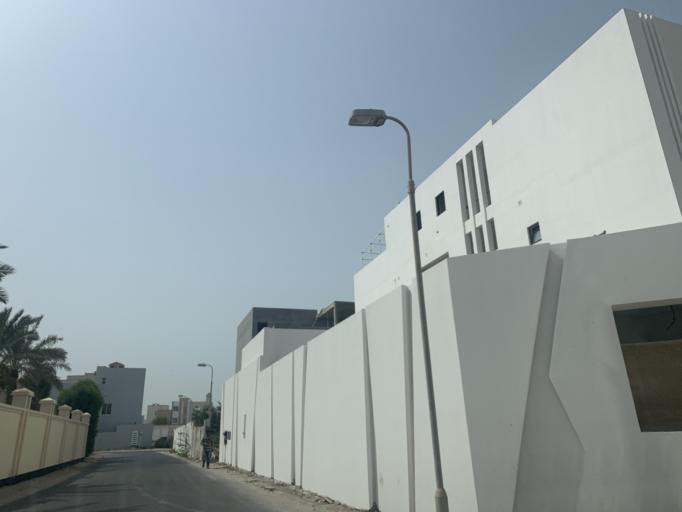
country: BH
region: Manama
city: Jidd Hafs
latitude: 26.1976
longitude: 50.4690
